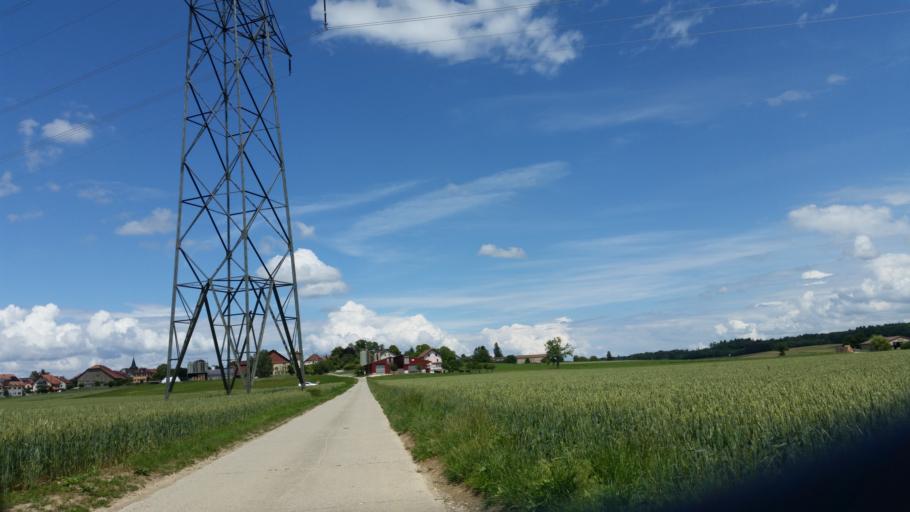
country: CH
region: Vaud
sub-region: Gros-de-Vaud District
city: Penthereaz
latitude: 46.6520
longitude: 6.6027
